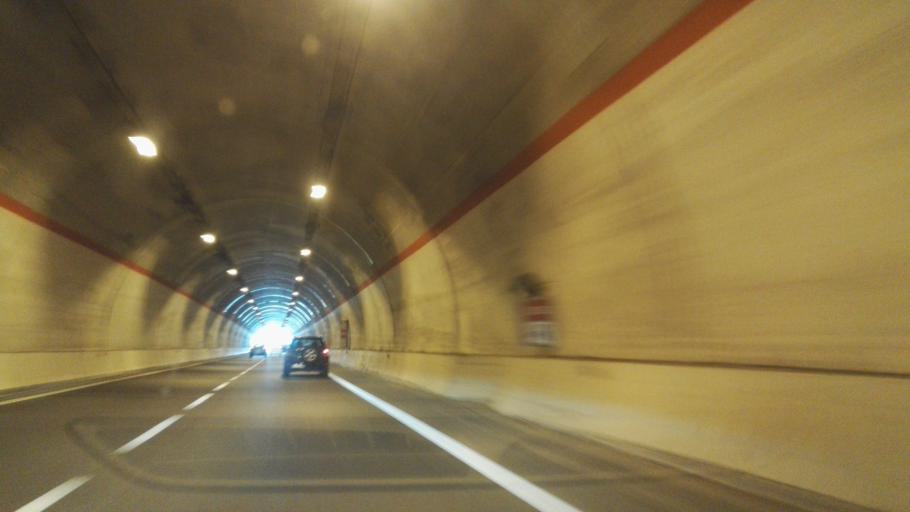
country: IT
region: Calabria
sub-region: Provincia di Catanzaro
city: Roccelletta
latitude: 38.8272
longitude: 16.5651
